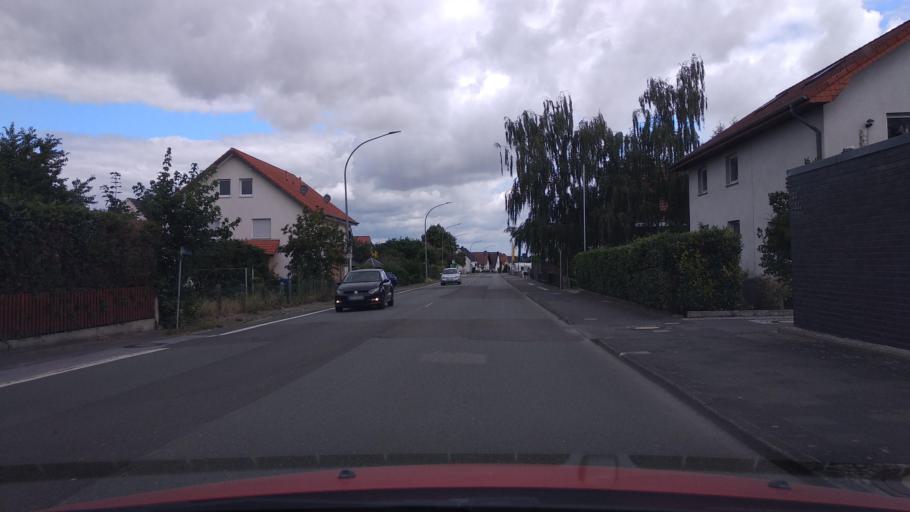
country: DE
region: North Rhine-Westphalia
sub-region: Regierungsbezirk Detmold
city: Paderborn
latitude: 51.6538
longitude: 8.7177
